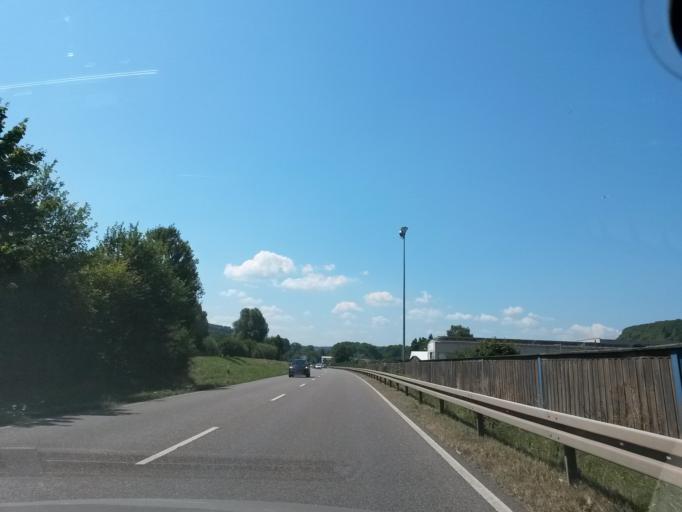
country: DE
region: Baden-Wuerttemberg
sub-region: Karlsruhe Region
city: Muhlacker
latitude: 48.9362
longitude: 8.8078
